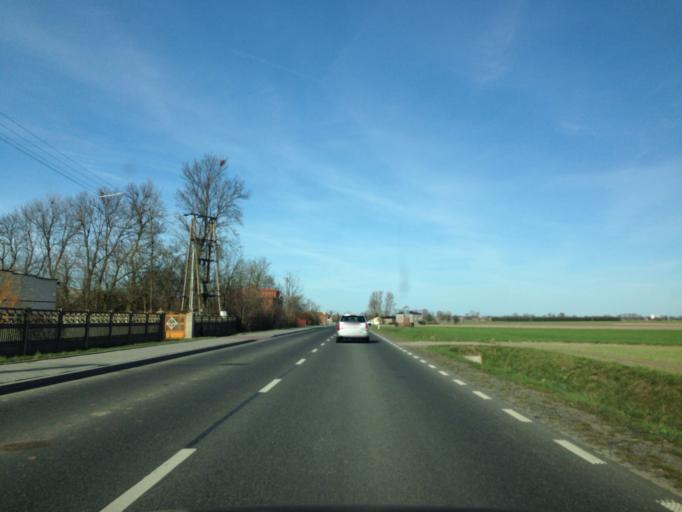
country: PL
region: Lodz Voivodeship
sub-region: Powiat leczycki
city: Leczyca
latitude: 52.0345
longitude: 19.1259
